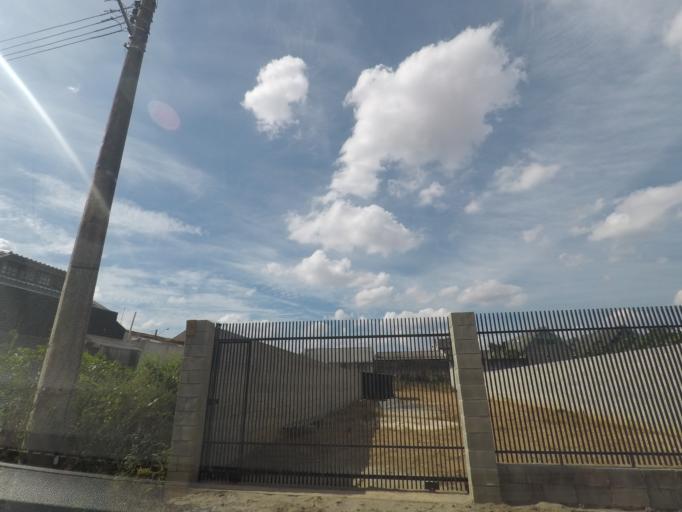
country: BR
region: Parana
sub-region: Curitiba
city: Curitiba
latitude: -25.4882
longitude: -49.2621
